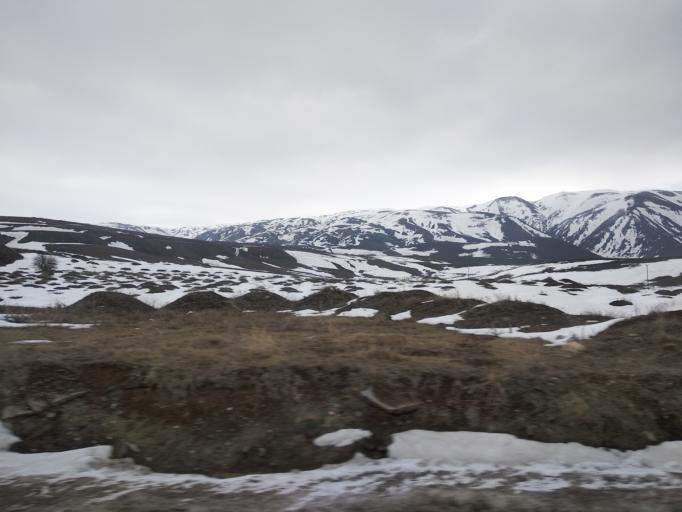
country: TR
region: Erzincan
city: Catalarmut
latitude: 39.8285
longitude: 39.3866
